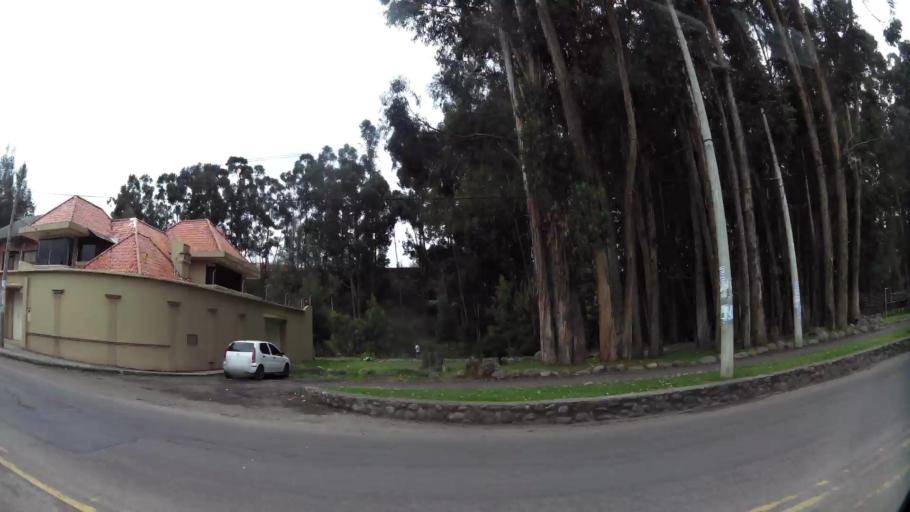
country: EC
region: Azuay
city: Cuenca
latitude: -2.9072
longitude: -79.0250
